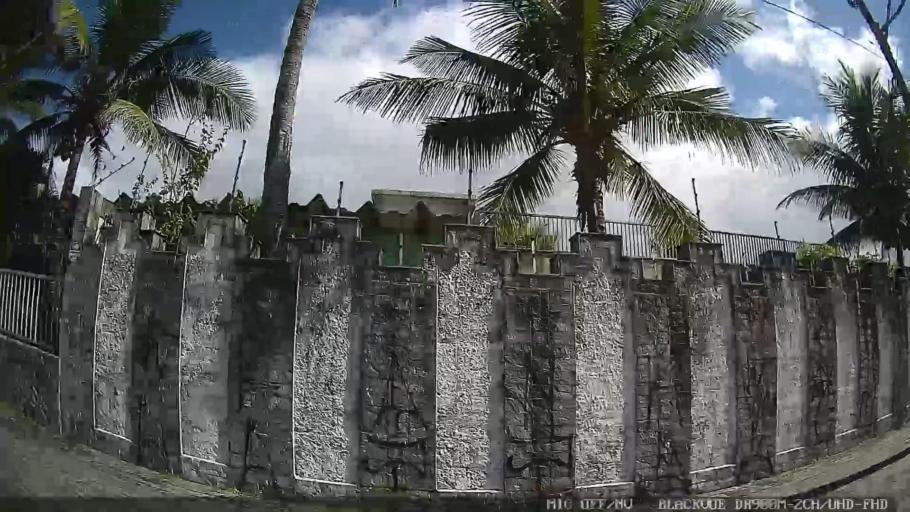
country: BR
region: Sao Paulo
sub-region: Peruibe
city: Peruibe
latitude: -24.2937
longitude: -46.9603
